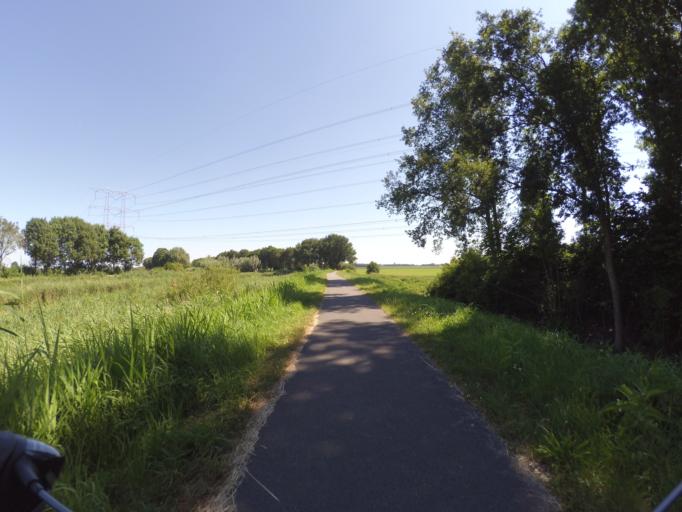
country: NL
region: North Brabant
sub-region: Gemeente Dongen
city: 's Gravenmoer
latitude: 51.6698
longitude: 4.9260
